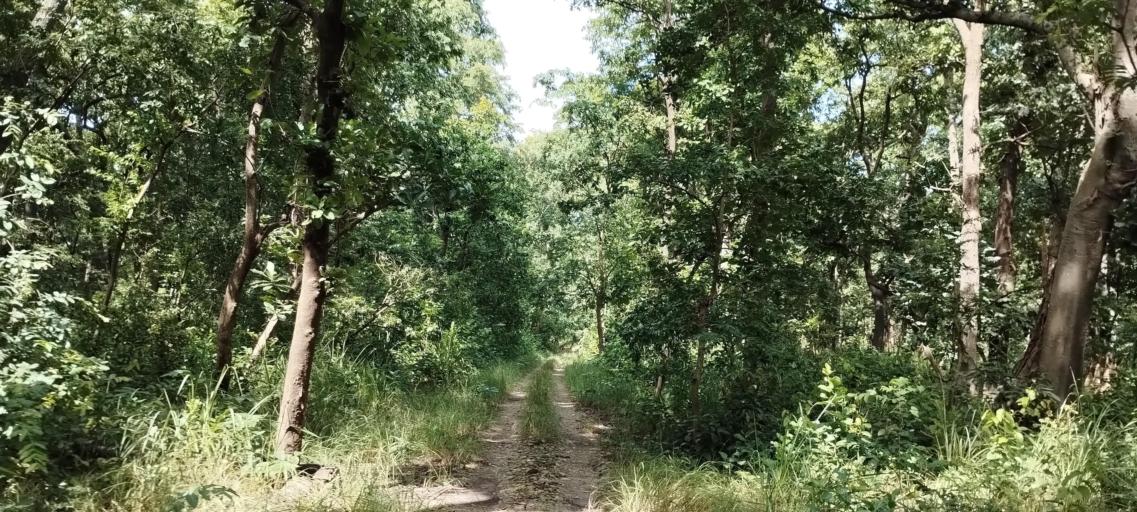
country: NP
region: Far Western
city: Tikapur
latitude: 28.5243
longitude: 81.2799
